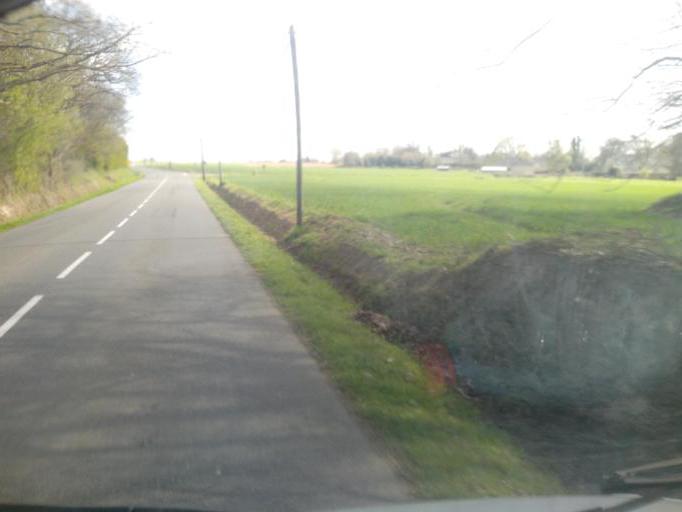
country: FR
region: Brittany
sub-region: Departement d'Ille-et-Vilaine
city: Paimpont
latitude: 48.0467
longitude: -2.1854
